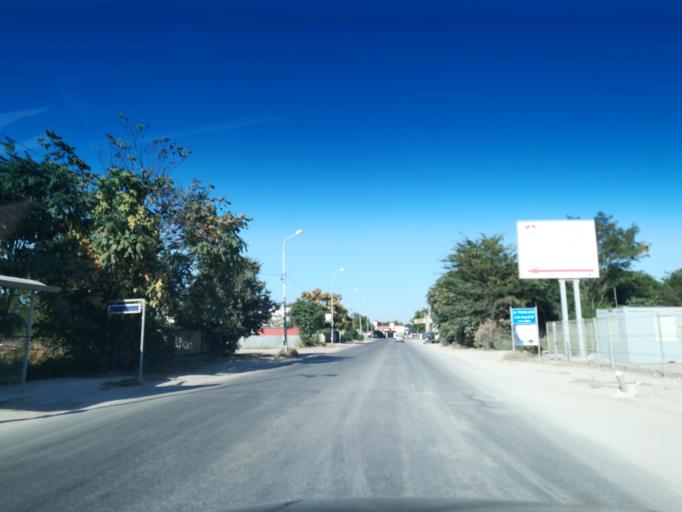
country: BG
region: Plovdiv
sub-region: Obshtina Plovdiv
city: Plovdiv
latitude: 42.1625
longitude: 24.7701
